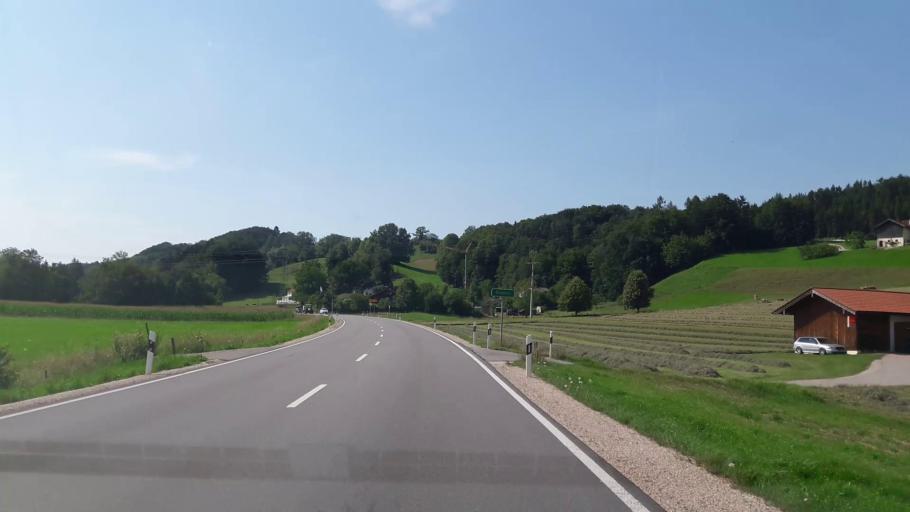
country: DE
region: Bavaria
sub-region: Upper Bavaria
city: Surberg
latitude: 47.8616
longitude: 12.7398
